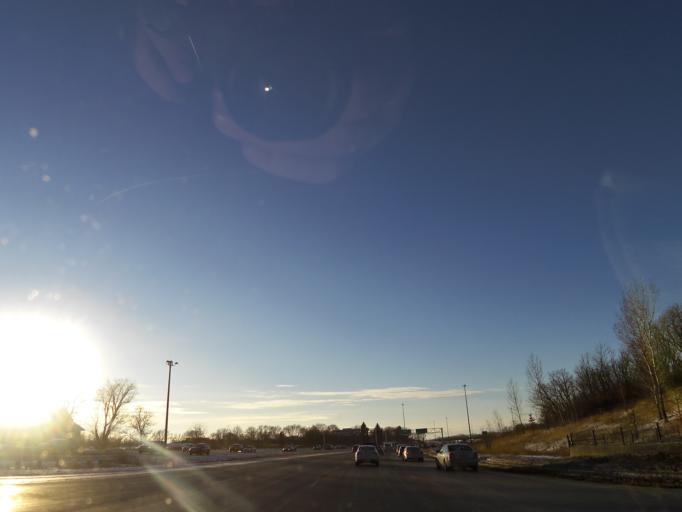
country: US
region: Minnesota
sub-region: Hennepin County
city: Eden Prairie
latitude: 44.8610
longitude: -93.4489
